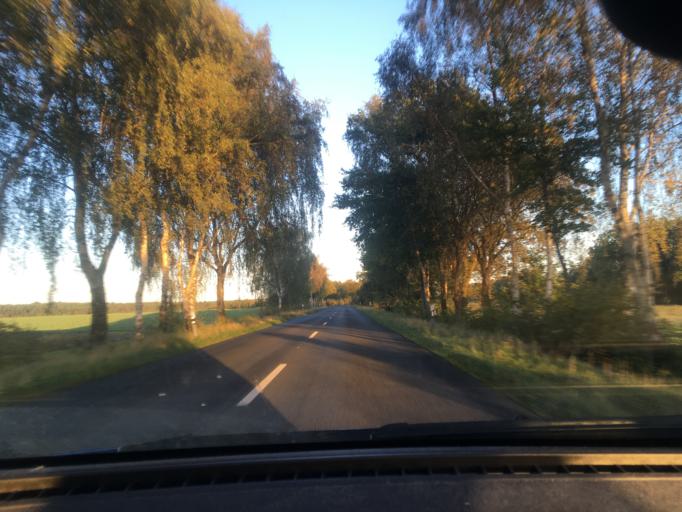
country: DE
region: Lower Saxony
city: Wendisch Evern
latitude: 53.2202
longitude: 10.4795
